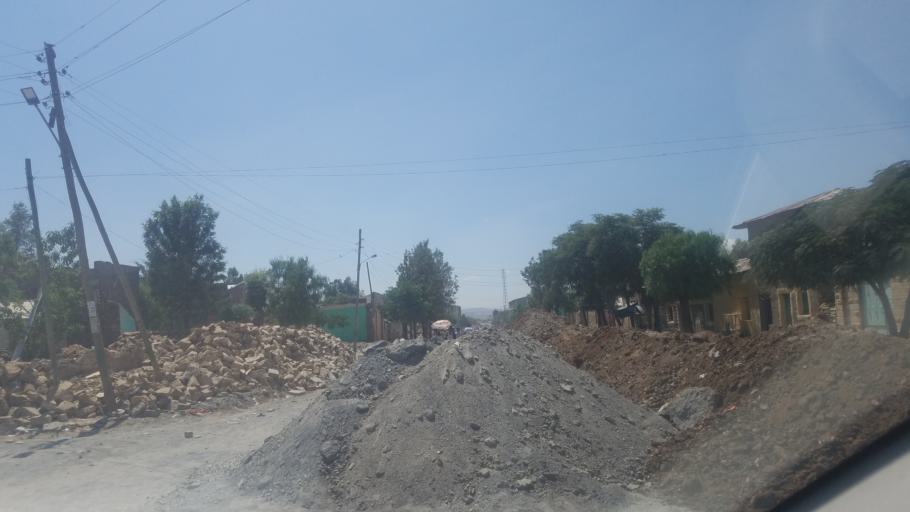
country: ET
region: Tigray
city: Mekele
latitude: 13.7934
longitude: 39.5992
